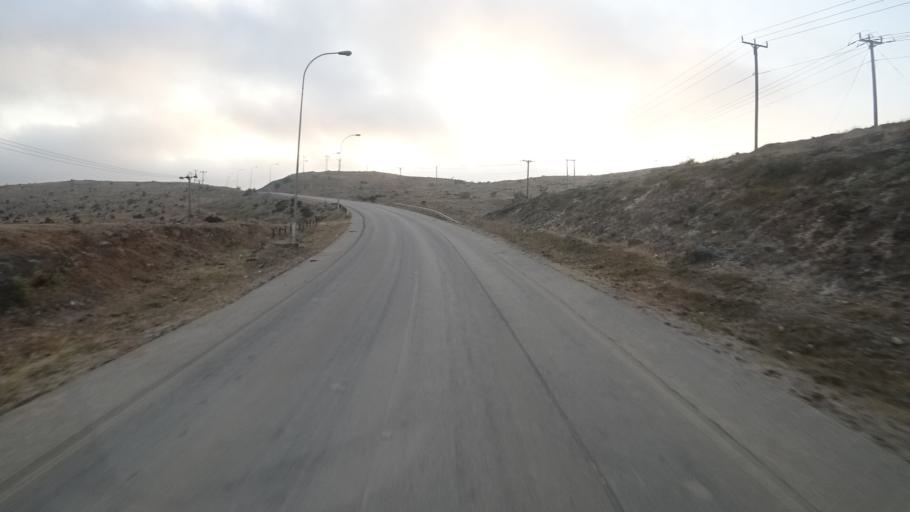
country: OM
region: Zufar
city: Salalah
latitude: 17.1290
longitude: 53.9567
